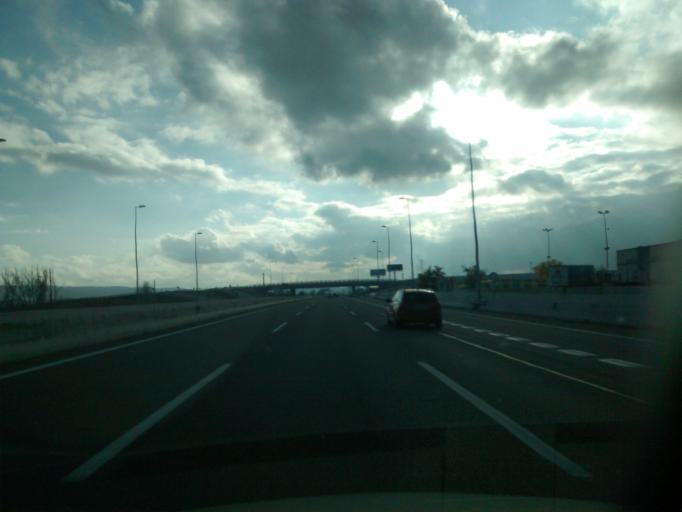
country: ES
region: Castille-La Mancha
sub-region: Provincia de Guadalajara
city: Alovera
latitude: 40.5962
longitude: -3.2215
